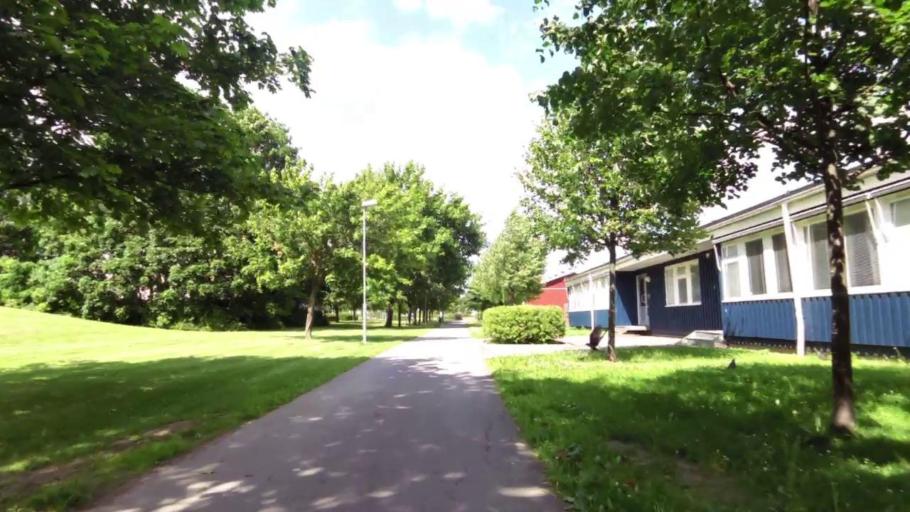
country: SE
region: OEstergoetland
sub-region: Linkopings Kommun
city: Linkoping
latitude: 58.4312
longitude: 15.5745
